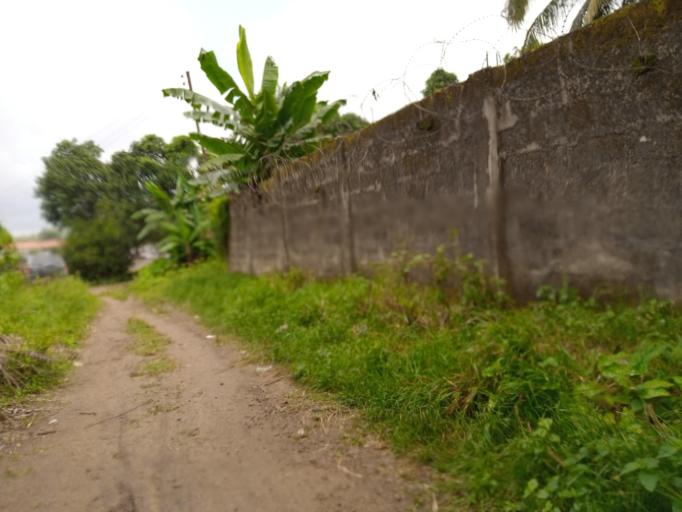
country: SL
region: Eastern Province
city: Kenema
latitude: 7.8577
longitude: -11.2014
